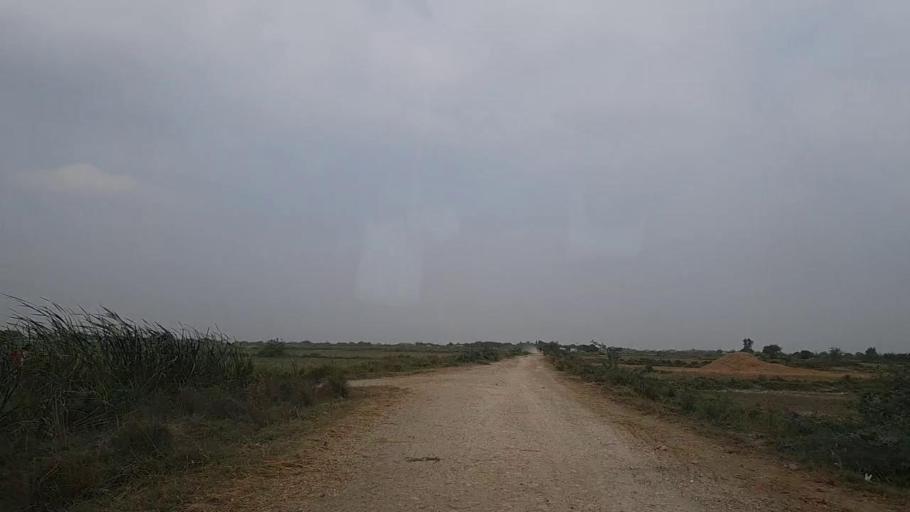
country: PK
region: Sindh
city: Mirpur Sakro
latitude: 24.5965
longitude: 67.6970
